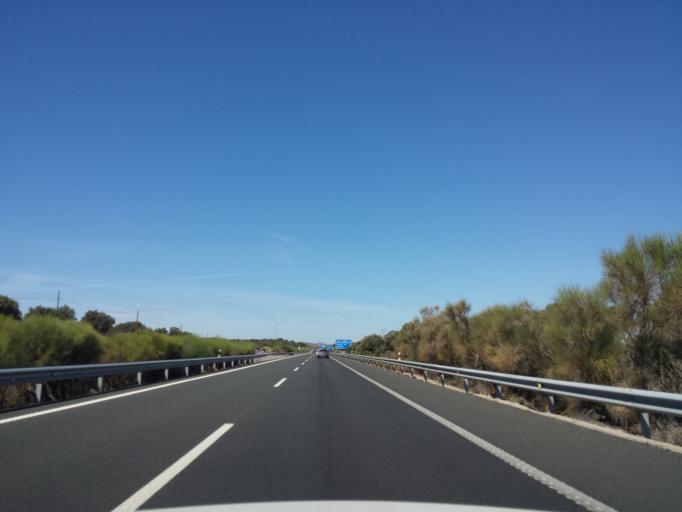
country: ES
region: Extremadura
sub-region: Provincia de Caceres
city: Peraleda de la Mata
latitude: 39.8900
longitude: -5.4472
